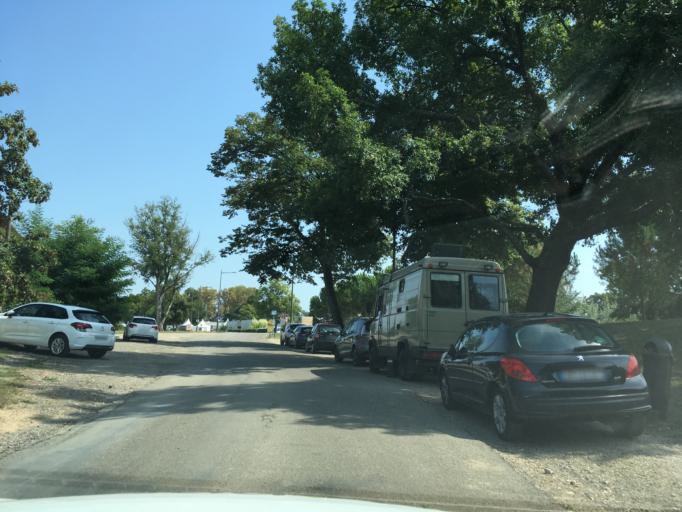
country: FR
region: Midi-Pyrenees
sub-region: Departement du Tarn-et-Garonne
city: Montauban
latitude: 44.0083
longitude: 1.3393
